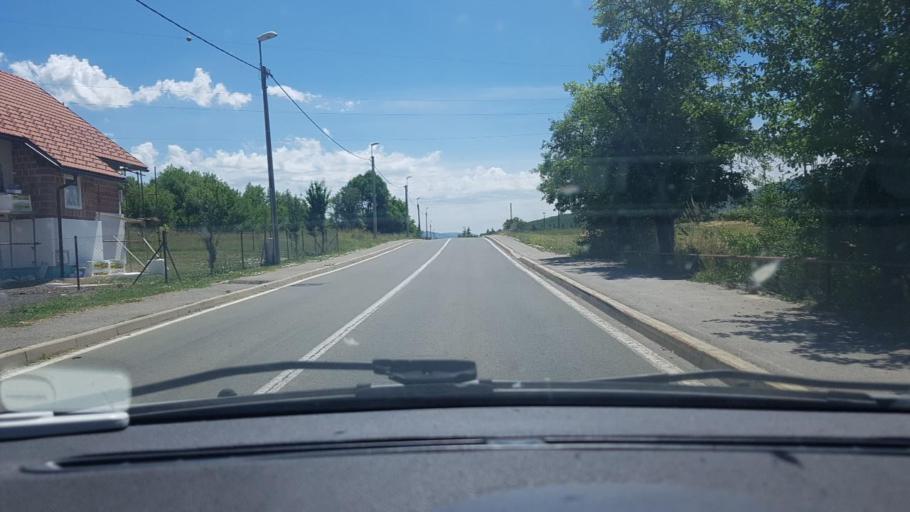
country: HR
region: Licko-Senjska
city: Otocac
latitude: 44.8643
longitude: 15.2592
